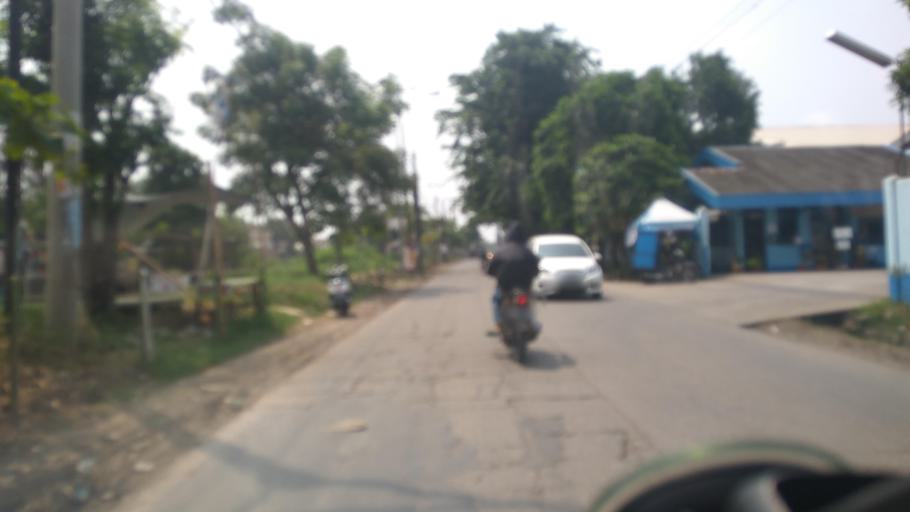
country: ID
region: West Java
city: Bekasi
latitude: -6.2092
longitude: 107.0307
